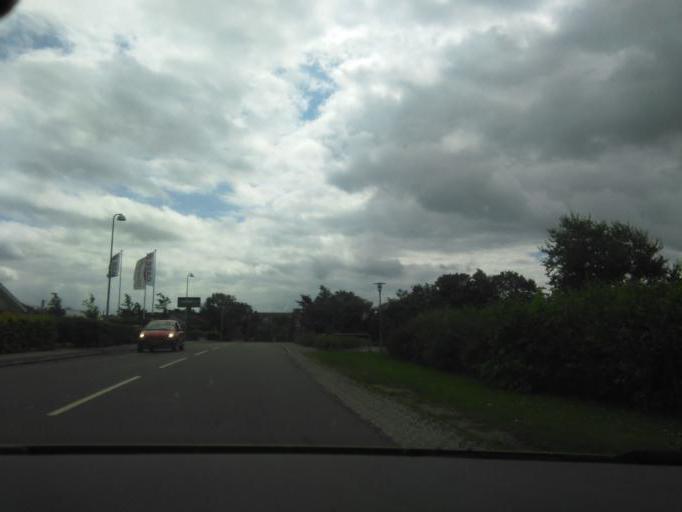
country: DK
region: Zealand
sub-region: Kalundborg Kommune
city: Gorlev
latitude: 55.5452
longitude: 11.2233
